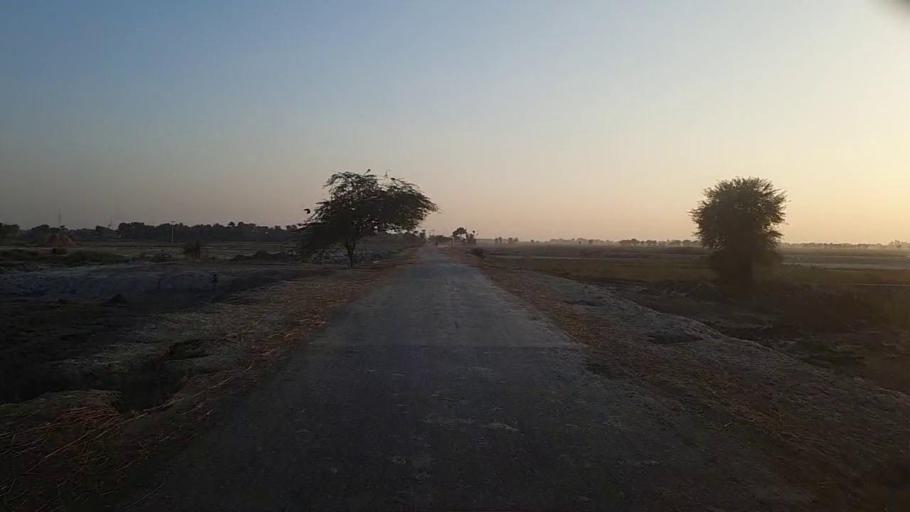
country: PK
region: Sindh
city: Khairpur Nathan Shah
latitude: 27.1745
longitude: 67.7337
